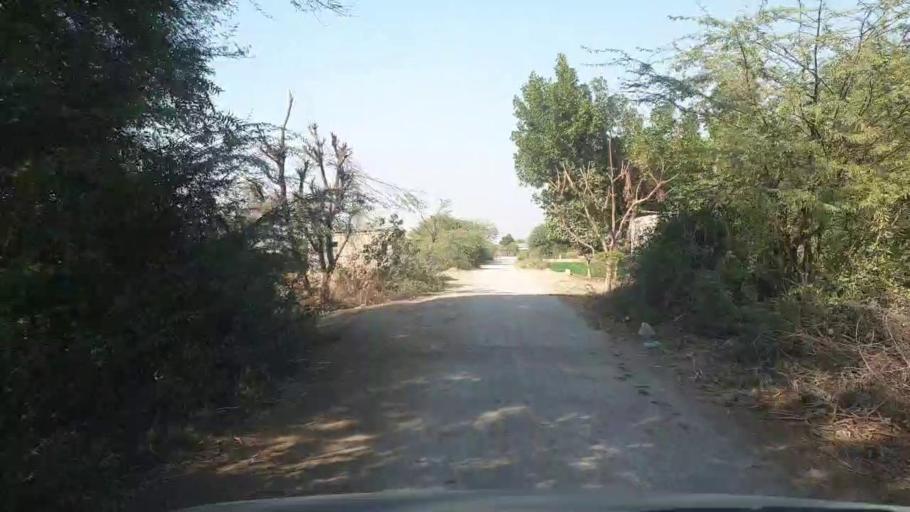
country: PK
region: Sindh
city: Chambar
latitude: 25.3081
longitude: 68.8457
